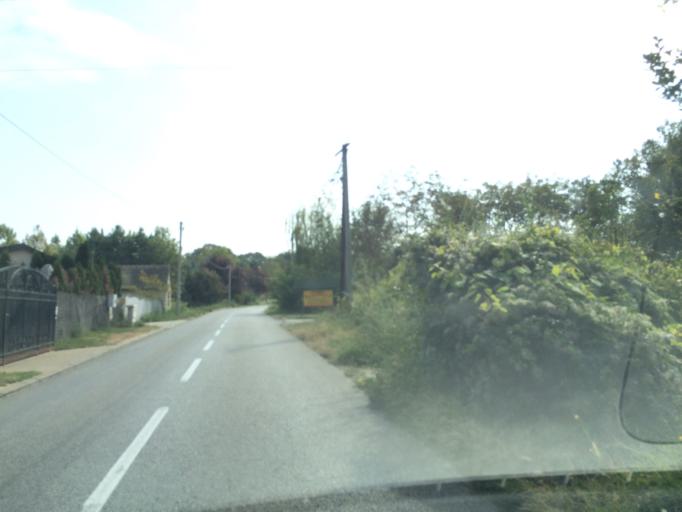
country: RS
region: Autonomna Pokrajina Vojvodina
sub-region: Juznobacki Okrug
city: Novi Sad
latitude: 45.2124
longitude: 19.8351
